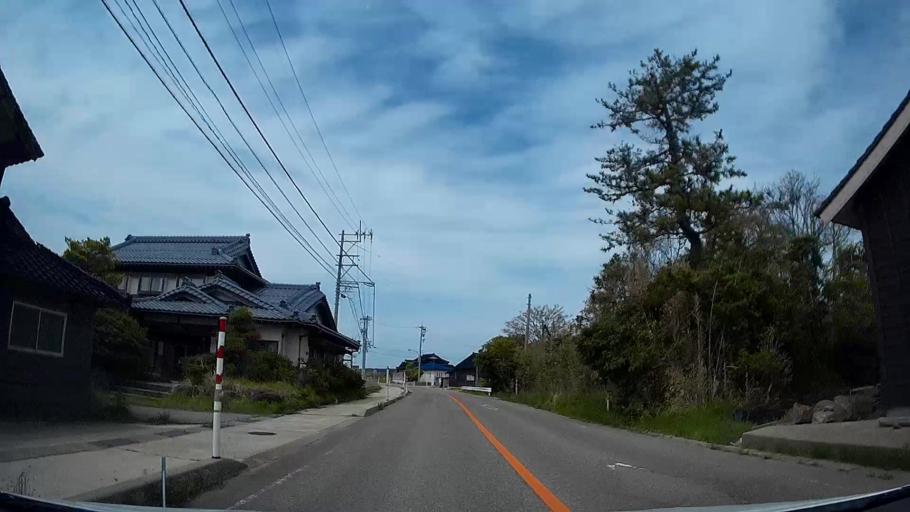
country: JP
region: Ishikawa
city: Hakui
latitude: 37.0236
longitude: 136.7476
